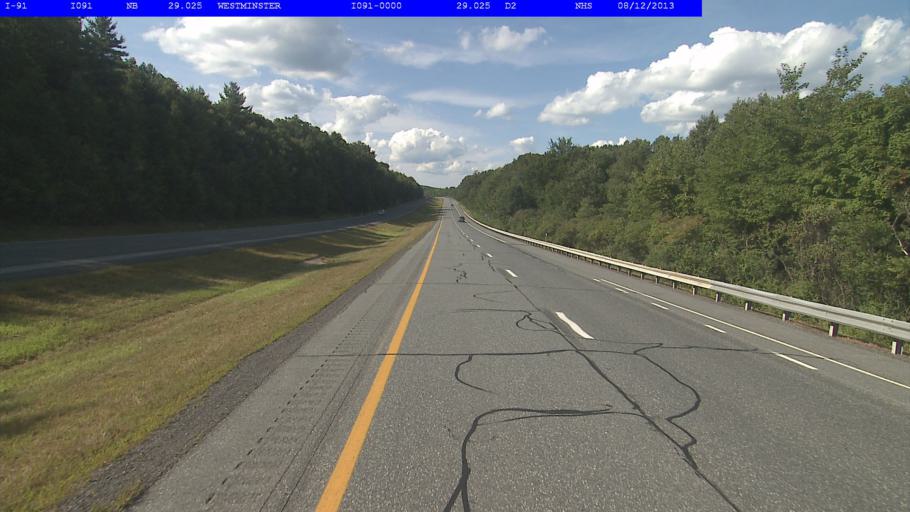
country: US
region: Vermont
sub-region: Windham County
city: Bellows Falls
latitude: 43.0974
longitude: -72.4539
